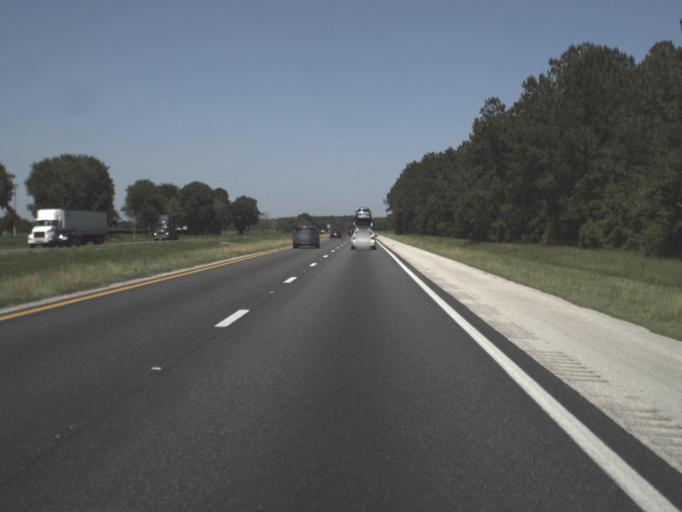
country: US
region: Florida
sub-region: Duval County
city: Baldwin
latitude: 30.2957
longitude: -81.9431
